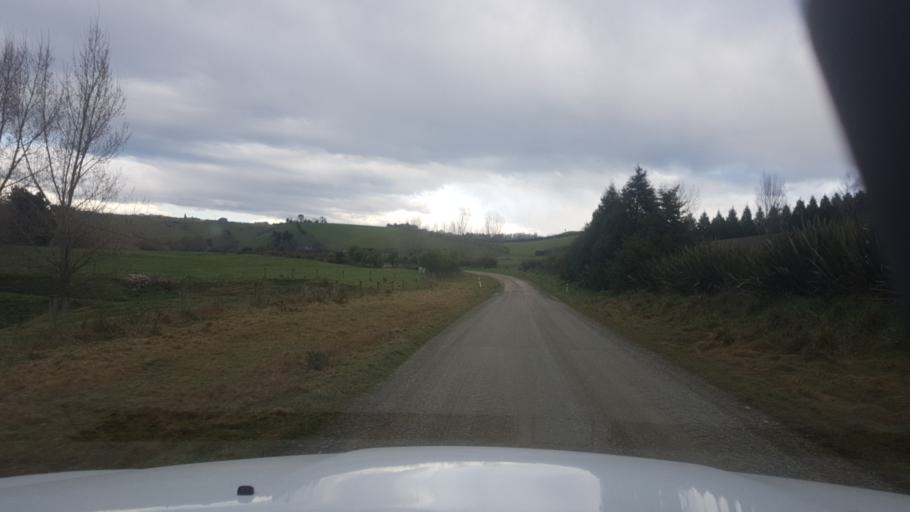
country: NZ
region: Canterbury
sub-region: Timaru District
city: Pleasant Point
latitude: -44.3417
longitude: 171.1631
